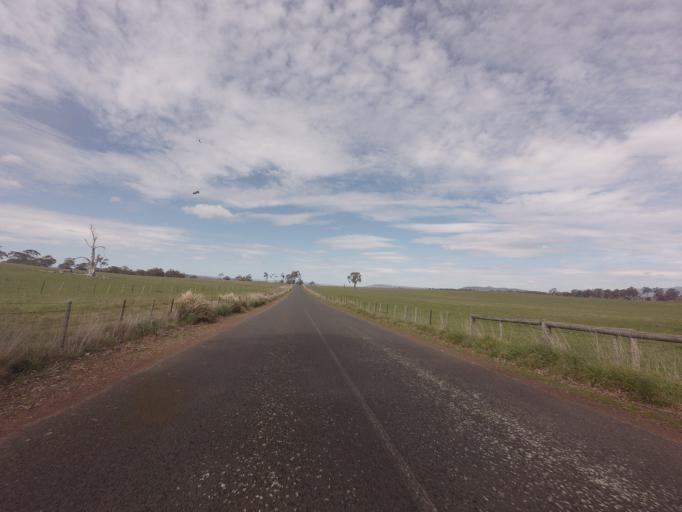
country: AU
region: Tasmania
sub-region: Northern Midlands
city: Evandale
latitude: -41.7869
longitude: 147.2422
